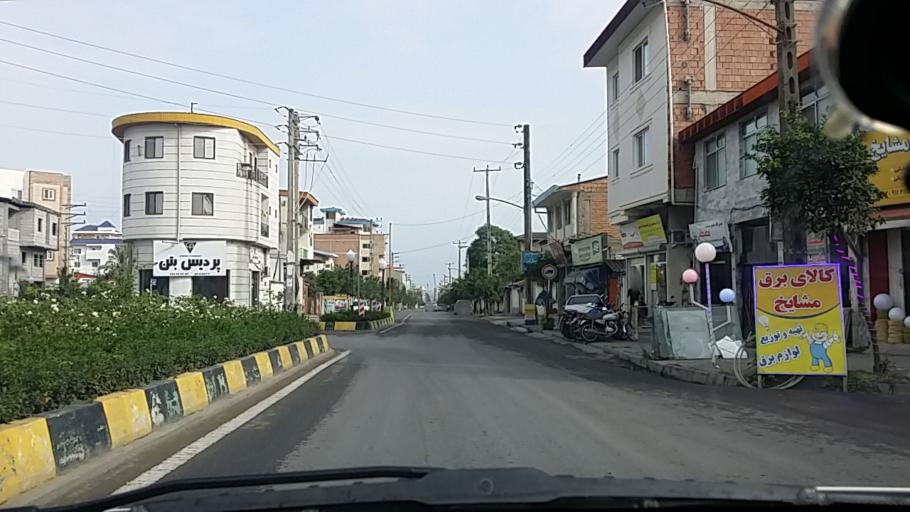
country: IR
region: Mazandaran
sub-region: Nowshahr
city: Nowshahr
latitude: 36.6389
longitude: 51.5081
